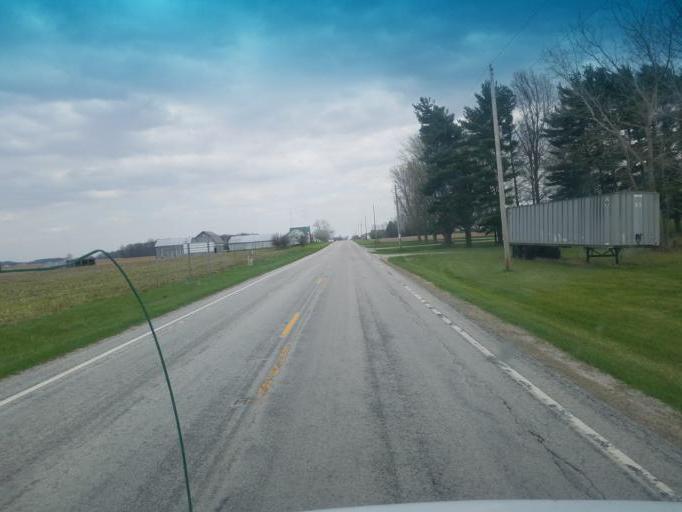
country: US
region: Ohio
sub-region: Seneca County
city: Tiffin
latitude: 40.9499
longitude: -83.1284
